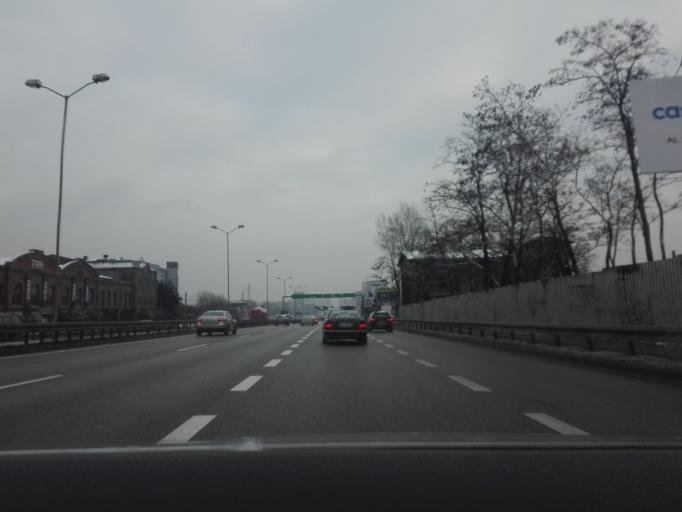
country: PL
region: Silesian Voivodeship
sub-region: Katowice
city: Katowice
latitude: 50.2691
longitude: 19.0032
